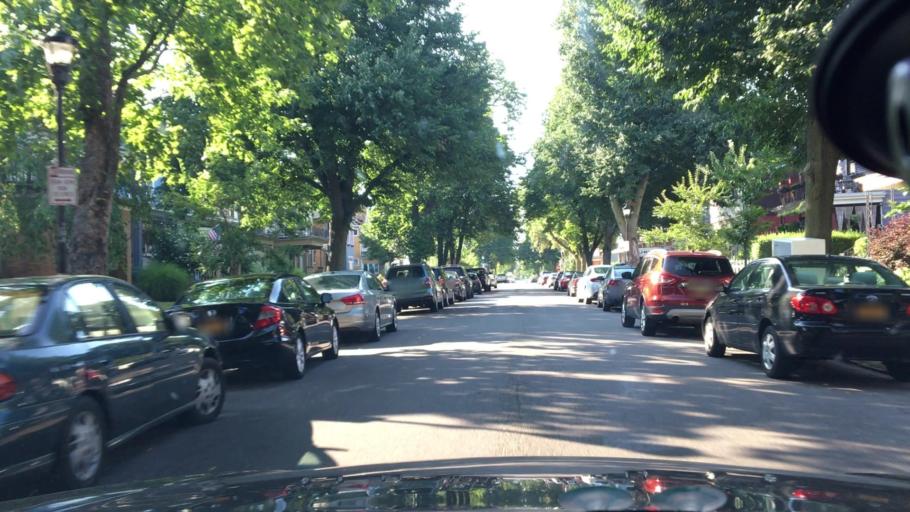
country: US
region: New York
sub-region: Erie County
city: Buffalo
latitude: 42.9044
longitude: -78.8968
